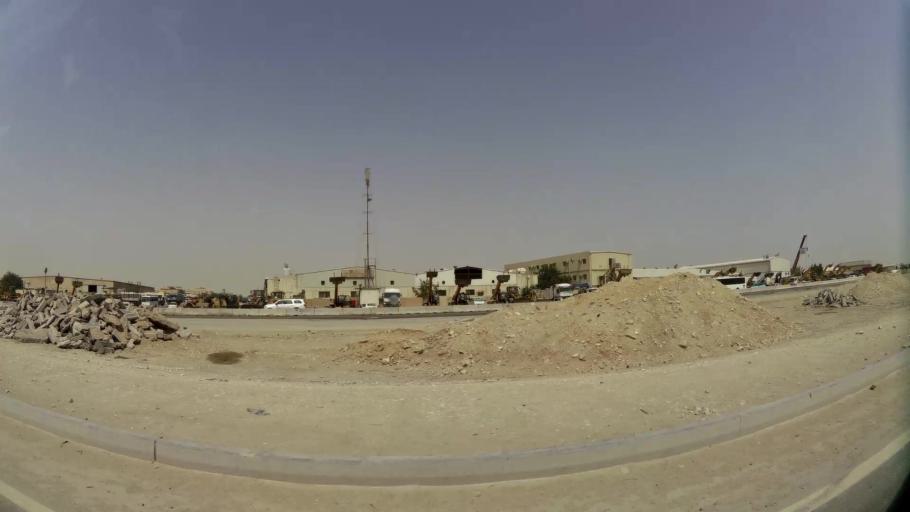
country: QA
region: Al Wakrah
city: Al Wukayr
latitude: 25.1887
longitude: 51.4454
